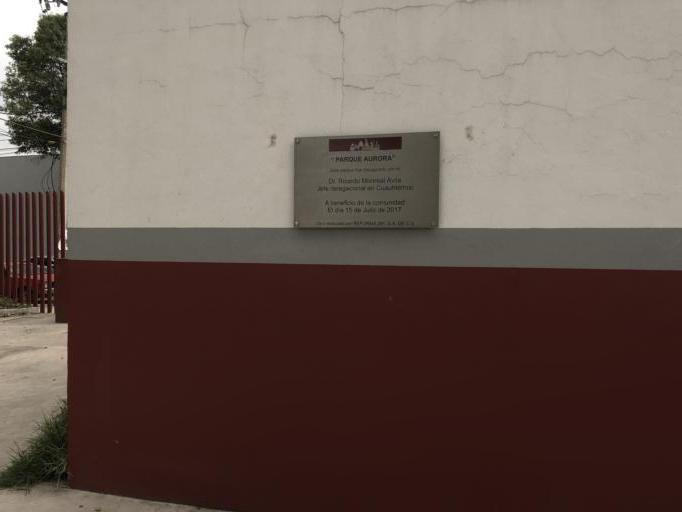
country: MX
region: Mexico City
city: Cuauhtemoc
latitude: 19.4541
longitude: -99.1296
